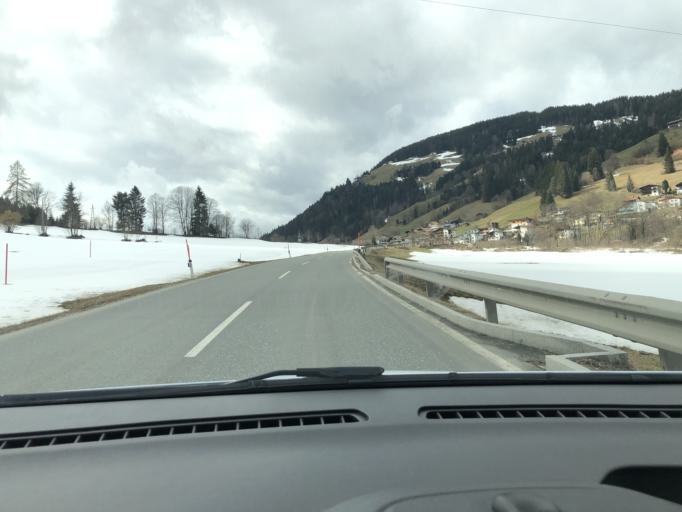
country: AT
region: Tyrol
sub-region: Politischer Bezirk Kufstein
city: Worgl
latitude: 47.4469
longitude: 12.0617
